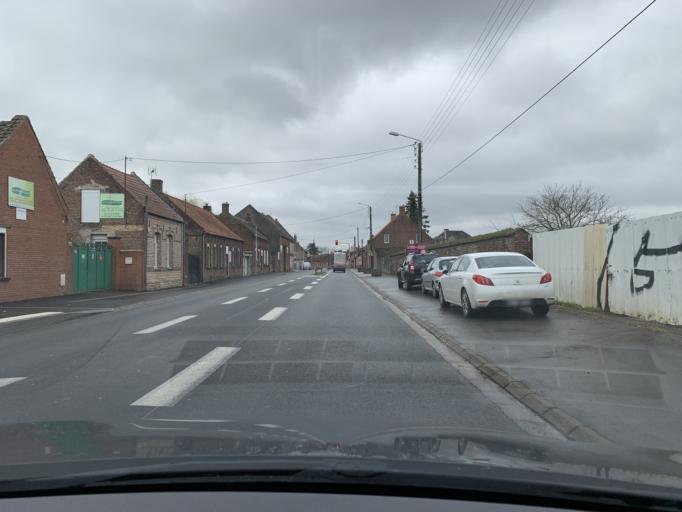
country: FR
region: Nord-Pas-de-Calais
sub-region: Departement du Nord
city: Iwuy
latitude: 50.2370
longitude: 3.3211
